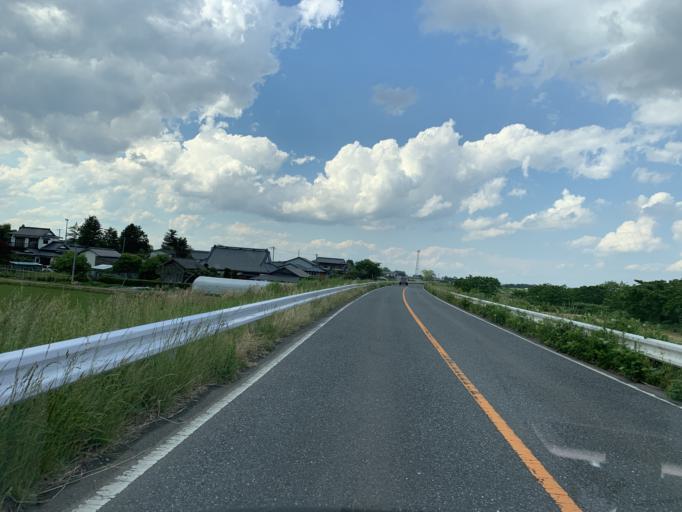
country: JP
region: Miyagi
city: Wakuya
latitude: 38.6351
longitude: 141.2044
